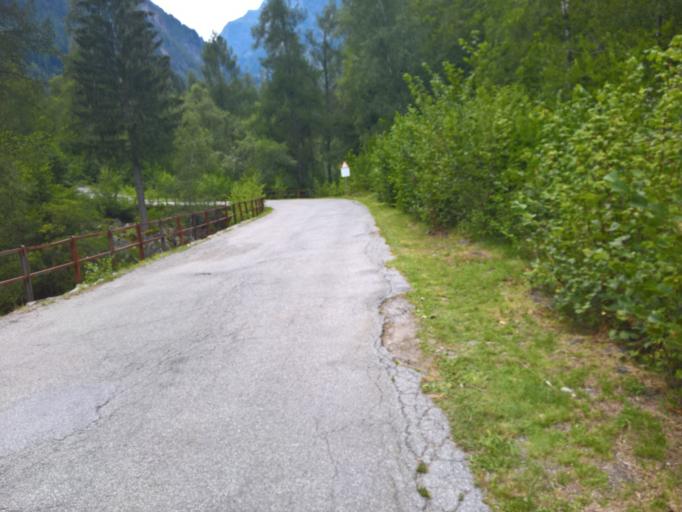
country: IT
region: Piedmont
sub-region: Provincia Verbano-Cusio-Ossola
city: Antrona Schieranco
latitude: 46.0558
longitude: 8.0971
